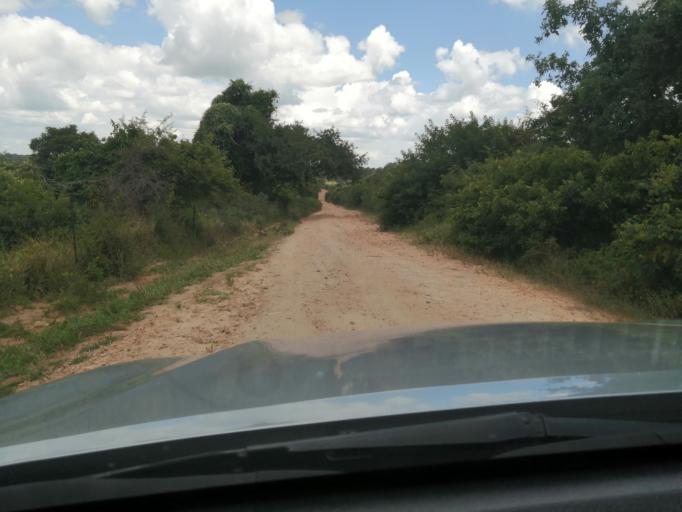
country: ZM
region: Lusaka
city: Lusaka
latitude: -15.3356
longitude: 28.0677
